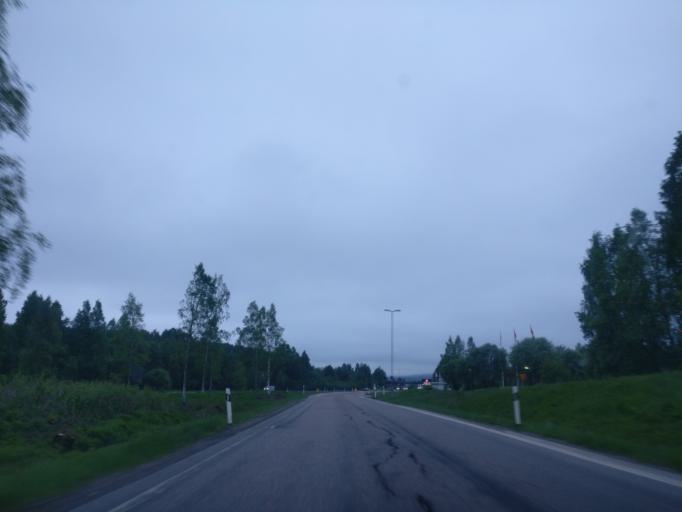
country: SE
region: Vaesternorrland
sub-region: Sundsvalls Kommun
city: Sundsvall
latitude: 62.4104
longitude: 17.3369
